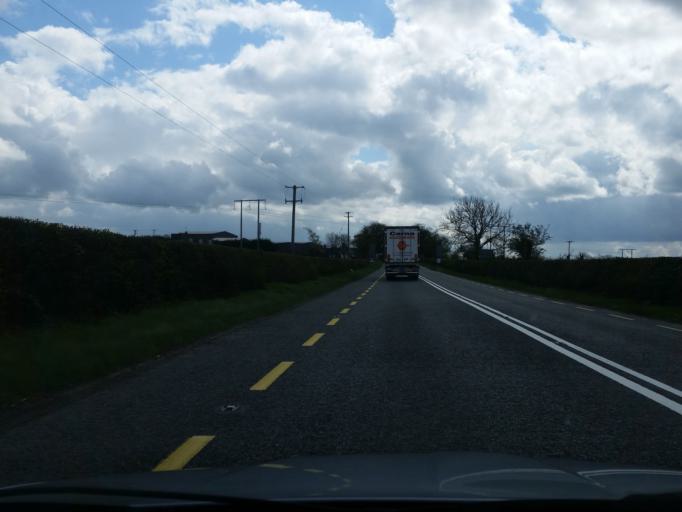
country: IE
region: Leinster
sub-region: An Mhi
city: Ratoath
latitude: 53.5557
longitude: -6.4382
